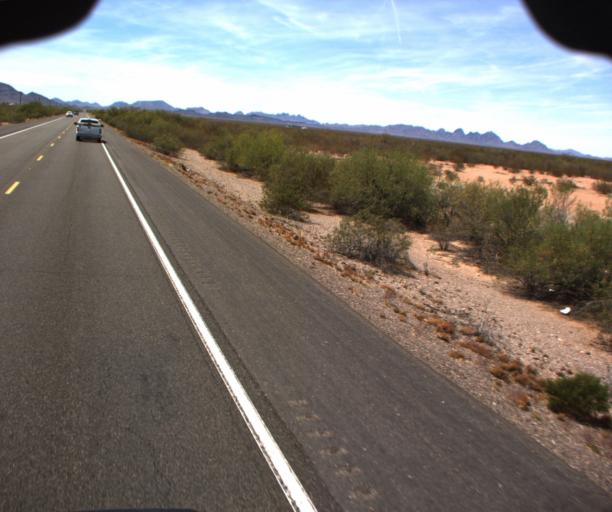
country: US
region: Arizona
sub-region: La Paz County
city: Salome
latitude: 33.7073
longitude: -113.8240
